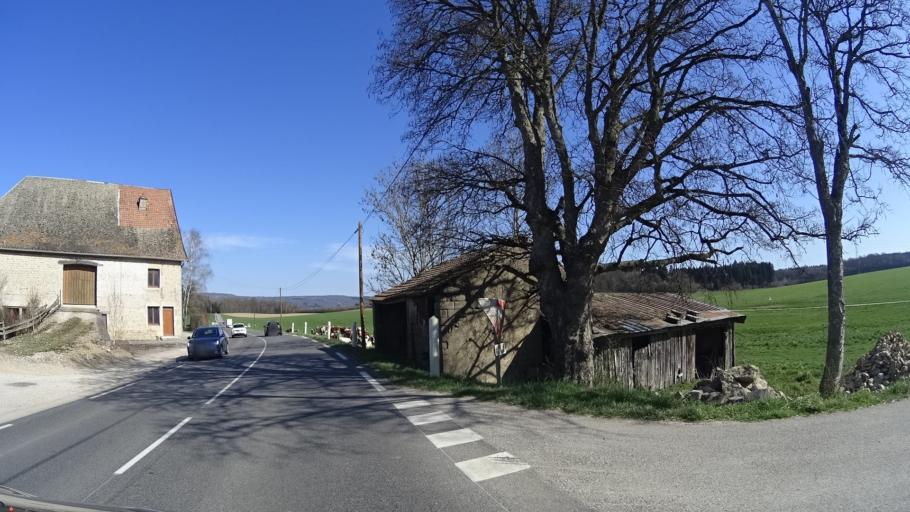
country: FR
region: Franche-Comte
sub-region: Departement du Doubs
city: Saone
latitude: 47.1955
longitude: 6.1082
